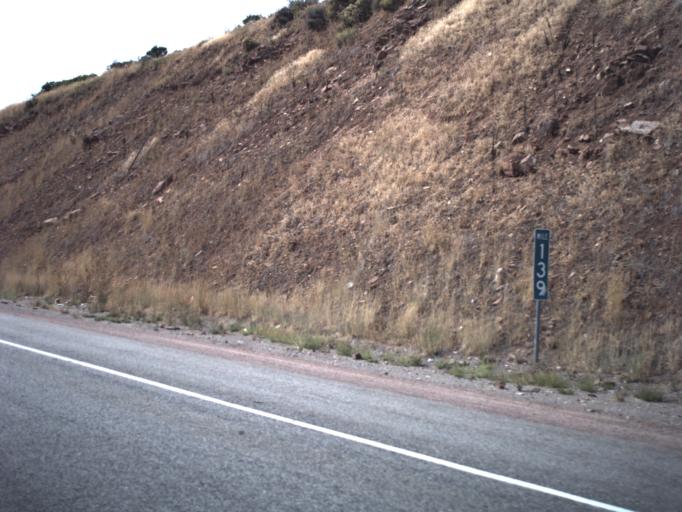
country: US
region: Utah
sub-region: Summit County
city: Summit Park
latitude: 40.7539
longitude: -111.6226
